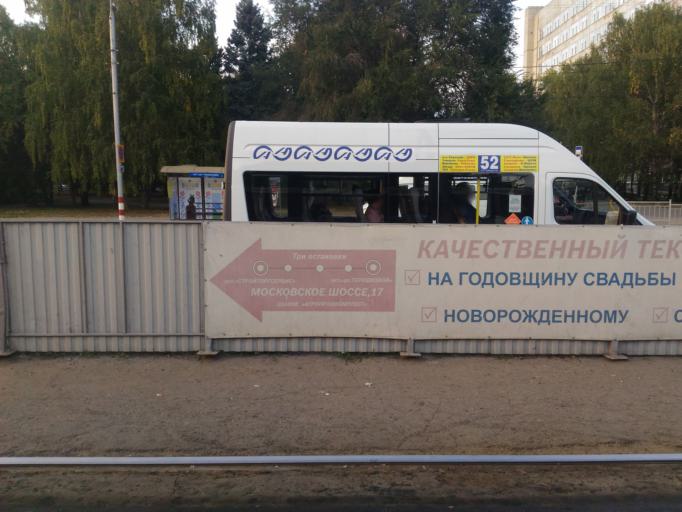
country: RU
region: Ulyanovsk
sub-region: Ulyanovskiy Rayon
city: Ulyanovsk
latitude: 54.3078
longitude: 48.3385
